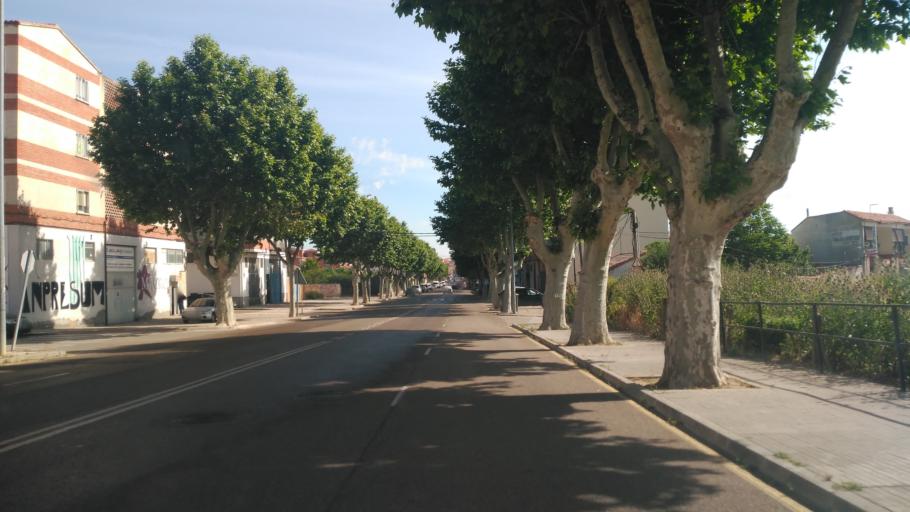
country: ES
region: Castille and Leon
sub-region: Provincia de Zamora
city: Zamora
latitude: 41.4911
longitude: -5.7436
